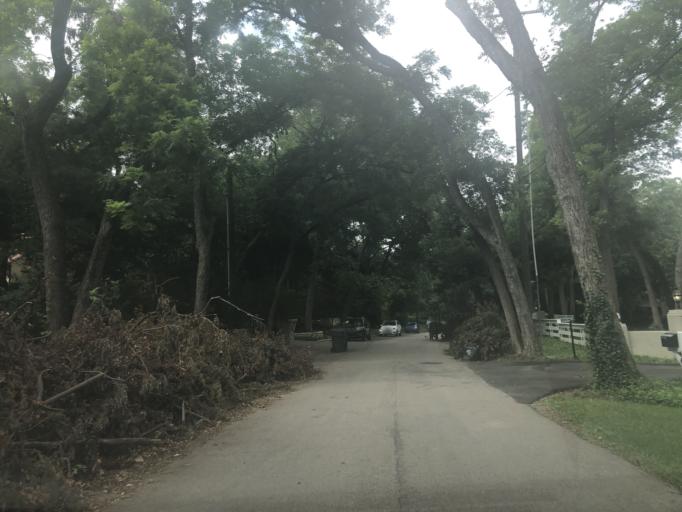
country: US
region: Texas
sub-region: Dallas County
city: University Park
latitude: 32.8609
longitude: -96.8347
